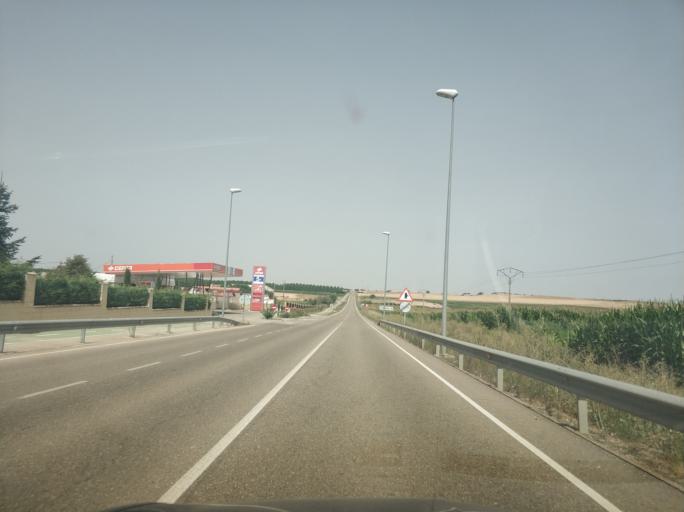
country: ES
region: Castille and Leon
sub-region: Provincia de Salamanca
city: Villamayor
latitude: 41.0181
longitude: -5.7166
